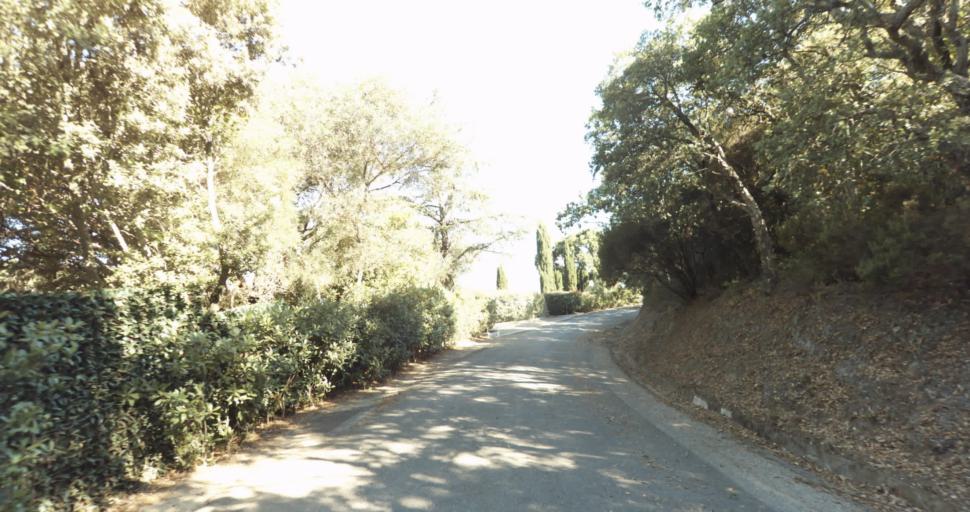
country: FR
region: Provence-Alpes-Cote d'Azur
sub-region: Departement du Var
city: Gassin
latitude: 43.2209
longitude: 6.5967
